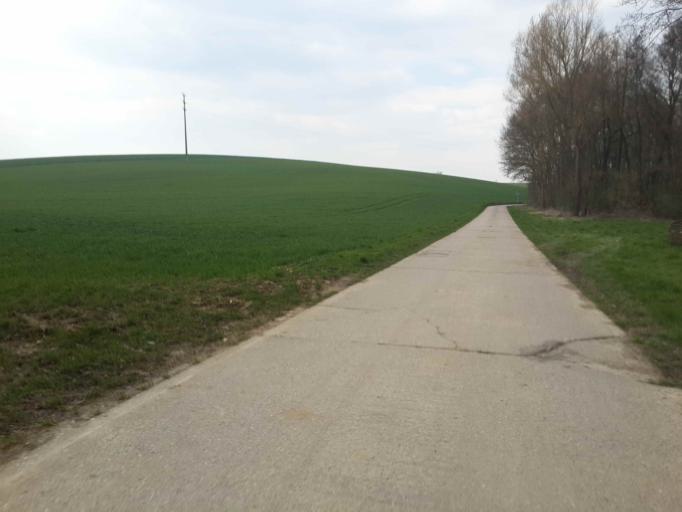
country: DE
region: Baden-Wuerttemberg
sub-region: Regierungsbezirk Stuttgart
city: Eppingen
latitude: 49.1570
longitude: 8.9373
